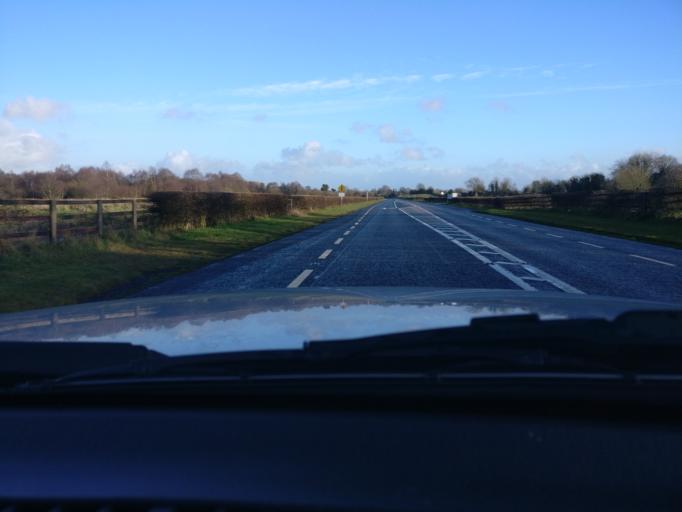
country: IE
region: Leinster
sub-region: An Iarmhi
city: An Muileann gCearr
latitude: 53.5520
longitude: -7.2623
